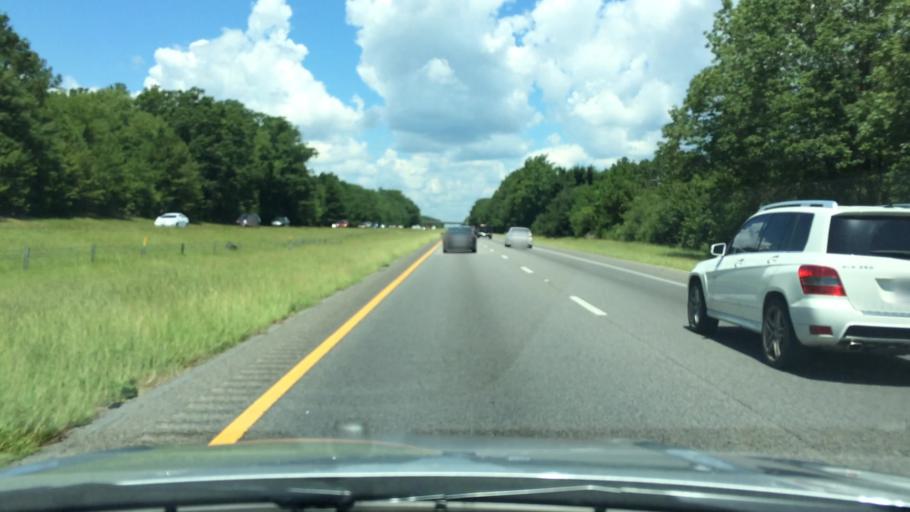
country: US
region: South Carolina
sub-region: Lexington County
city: Irmo
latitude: 34.1175
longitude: -81.1939
